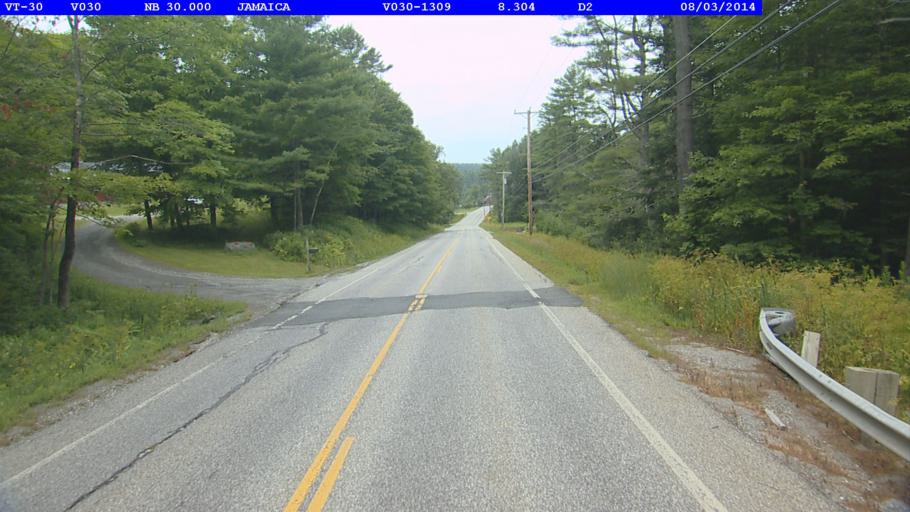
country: US
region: Vermont
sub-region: Windham County
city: Dover
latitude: 43.1445
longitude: -72.8313
